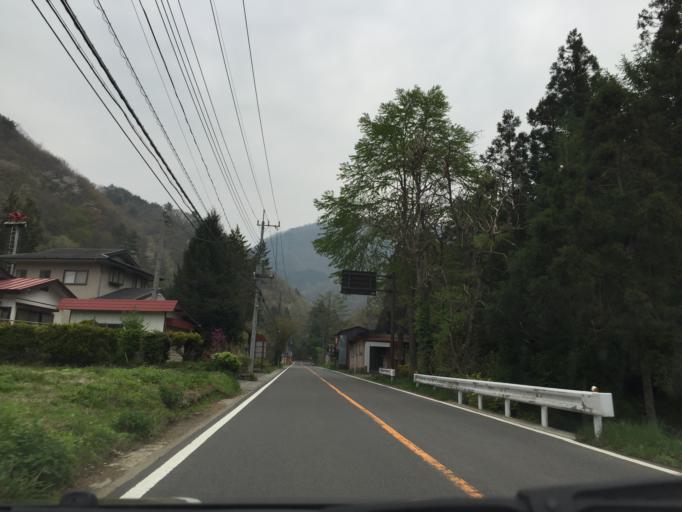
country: JP
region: Tochigi
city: Nikko
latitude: 36.9871
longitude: 139.7009
